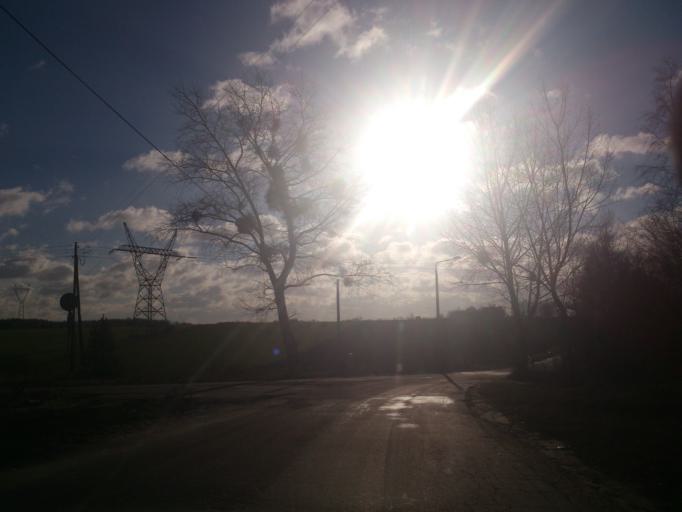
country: PL
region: Kujawsko-Pomorskie
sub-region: Powiat torunski
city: Lubicz Gorny
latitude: 53.0444
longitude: 18.8168
